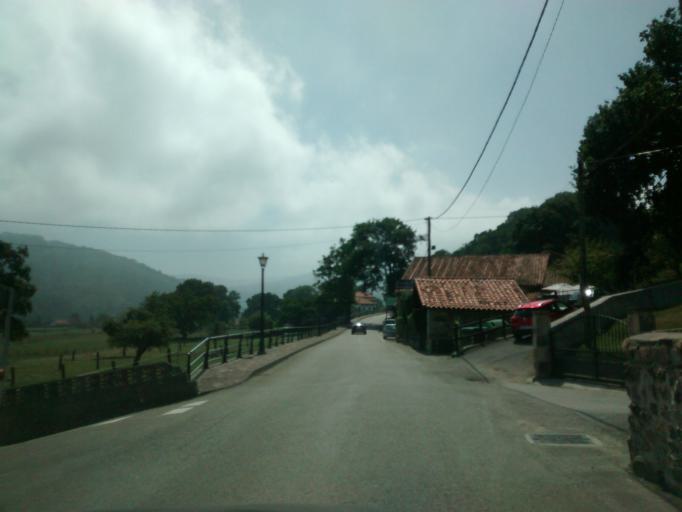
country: ES
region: Cantabria
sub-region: Provincia de Cantabria
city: Ruente
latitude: 43.2638
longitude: -4.2492
